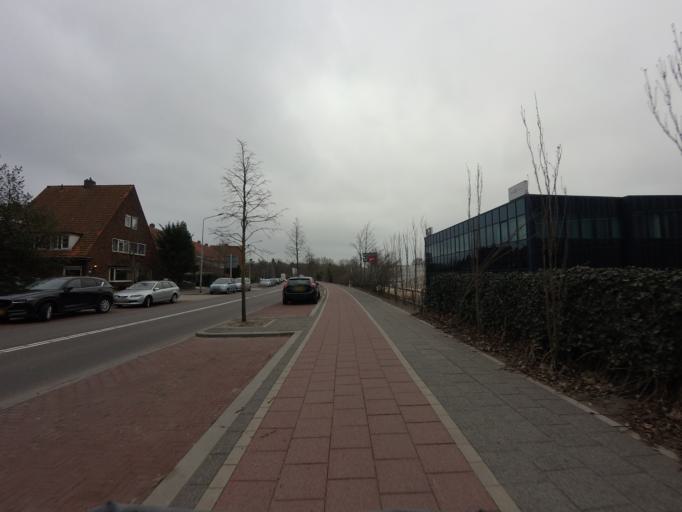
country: NL
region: North Holland
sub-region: Gemeente Hilversum
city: Hilversum
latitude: 52.2225
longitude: 5.1514
